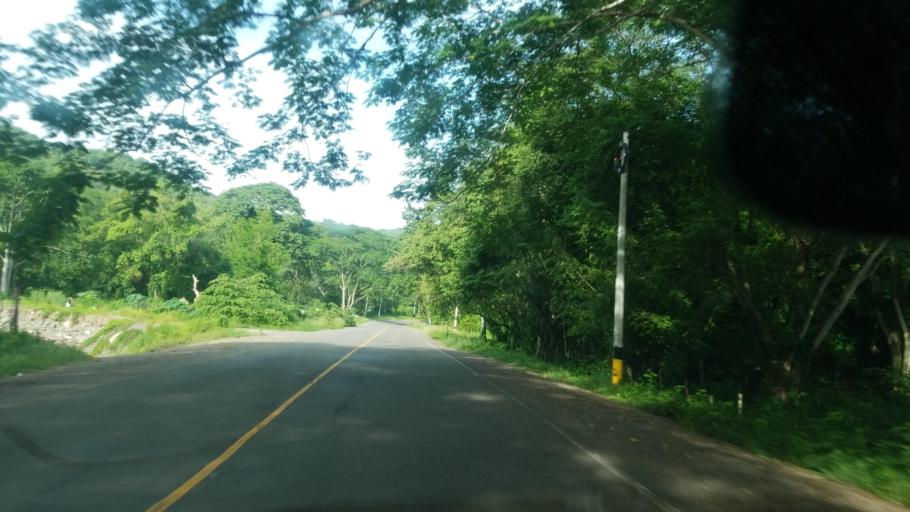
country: HN
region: Santa Barbara
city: Trinidad
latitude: 15.1343
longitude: -88.2206
